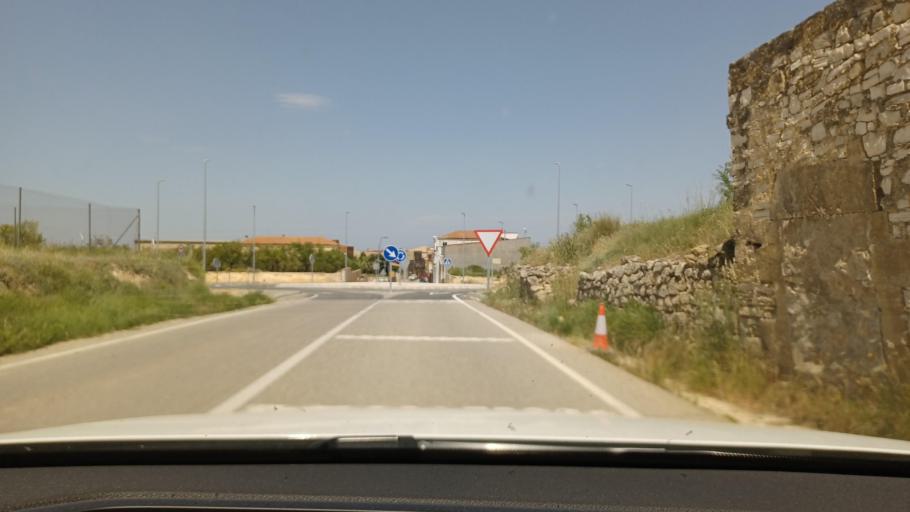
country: ES
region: Catalonia
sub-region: Provincia de Tarragona
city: Vilalba dels Arcs
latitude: 41.1165
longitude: 0.4092
